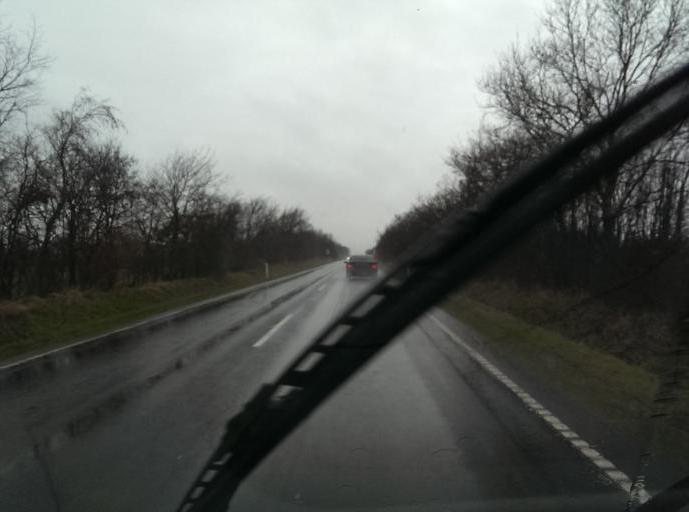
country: DK
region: South Denmark
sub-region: Varde Kommune
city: Olgod
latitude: 55.7120
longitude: 8.6093
